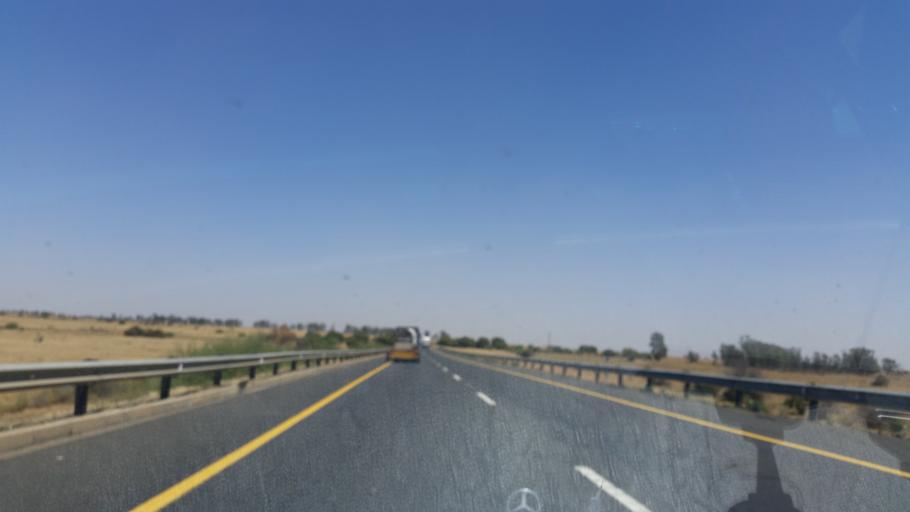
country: ZA
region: Orange Free State
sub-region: Lejweleputswa District Municipality
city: Winburg
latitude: -28.6334
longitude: 26.9010
